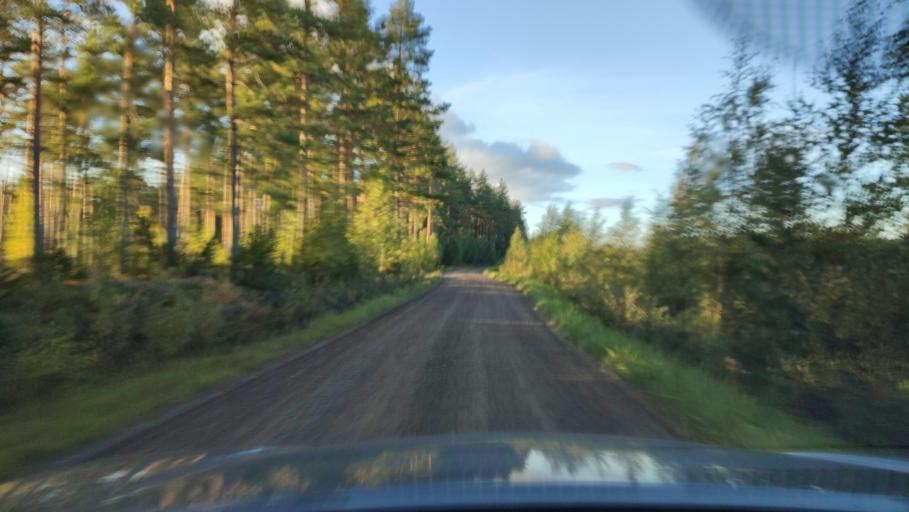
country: FI
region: Southern Ostrobothnia
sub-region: Suupohja
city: Karijoki
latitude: 62.2210
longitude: 21.5716
